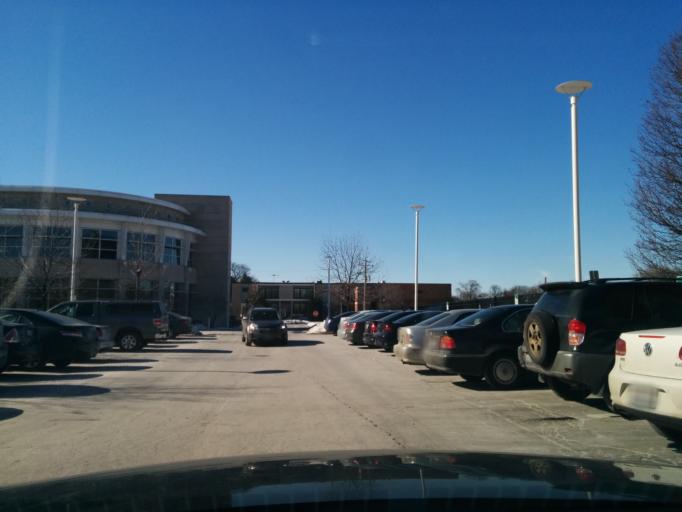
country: US
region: Illinois
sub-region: DuPage County
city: Elmhurst
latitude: 41.8990
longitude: -87.9436
